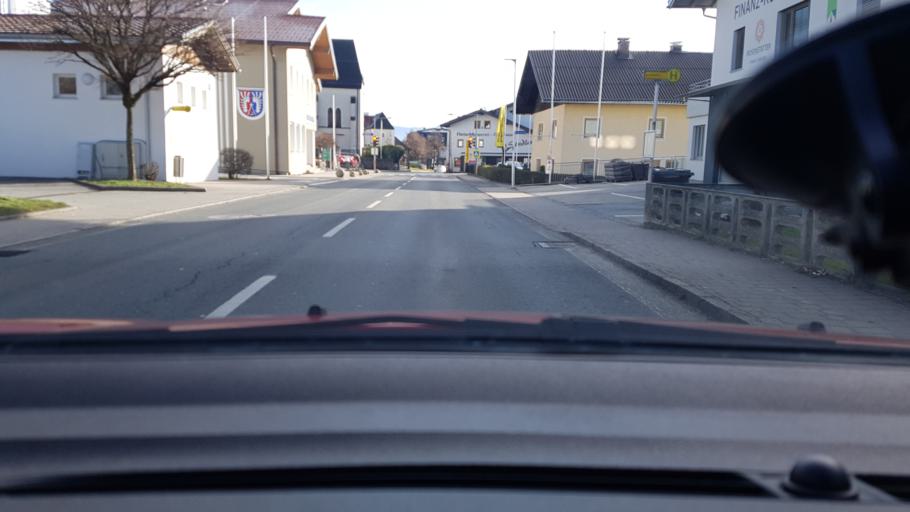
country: AT
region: Salzburg
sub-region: Politischer Bezirk Salzburg-Umgebung
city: Lamprechtshausen
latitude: 47.9930
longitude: 12.9559
